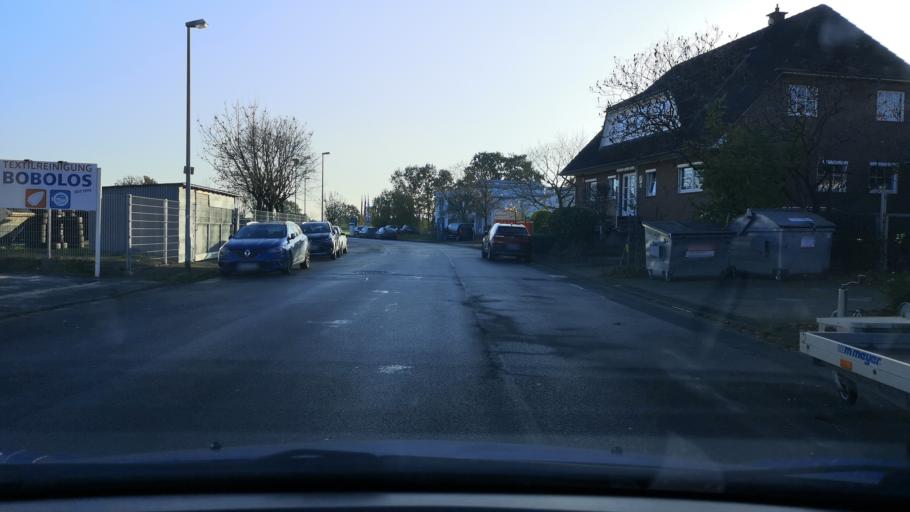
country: DE
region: Lower Saxony
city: Langenhagen
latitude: 52.4510
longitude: 9.7859
